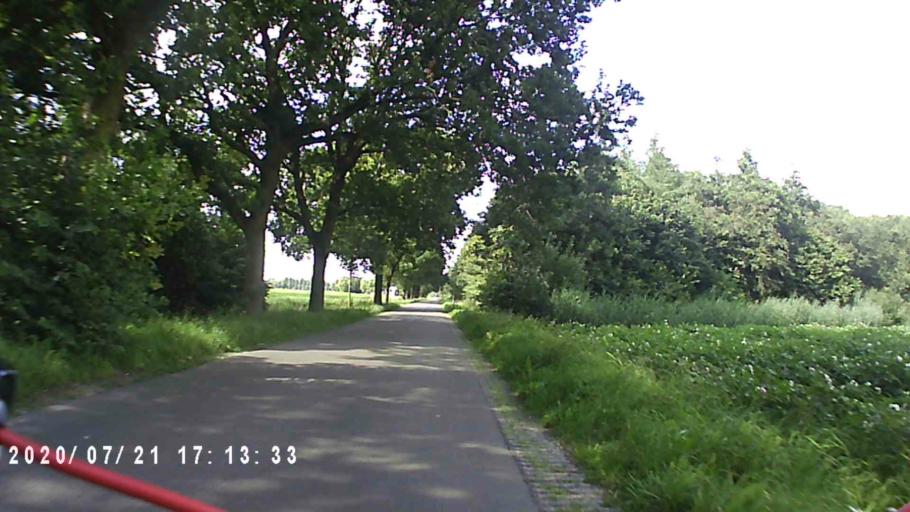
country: NL
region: Groningen
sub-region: Gemeente Hoogezand-Sappemeer
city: Hoogezand
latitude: 53.1384
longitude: 6.7578
